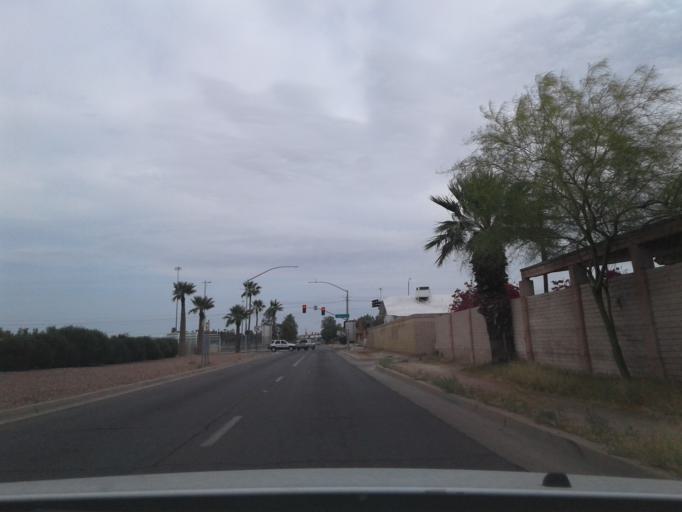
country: US
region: Arizona
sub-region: Maricopa County
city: Phoenix
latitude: 33.4460
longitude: -112.1077
